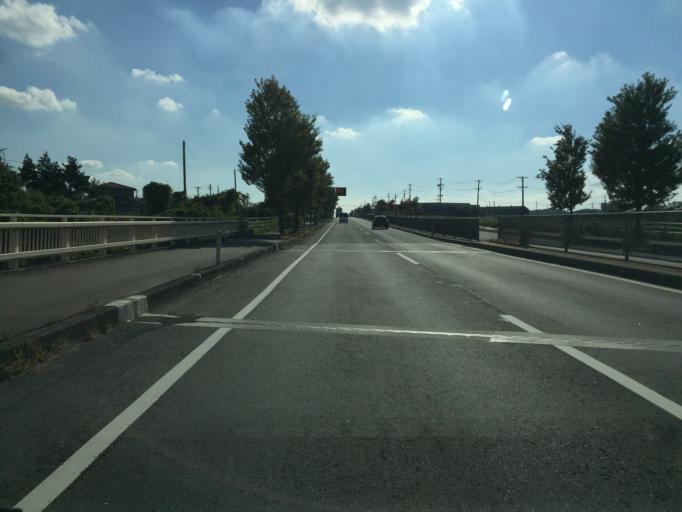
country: JP
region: Fukushima
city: Motomiya
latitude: 37.4995
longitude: 140.3901
